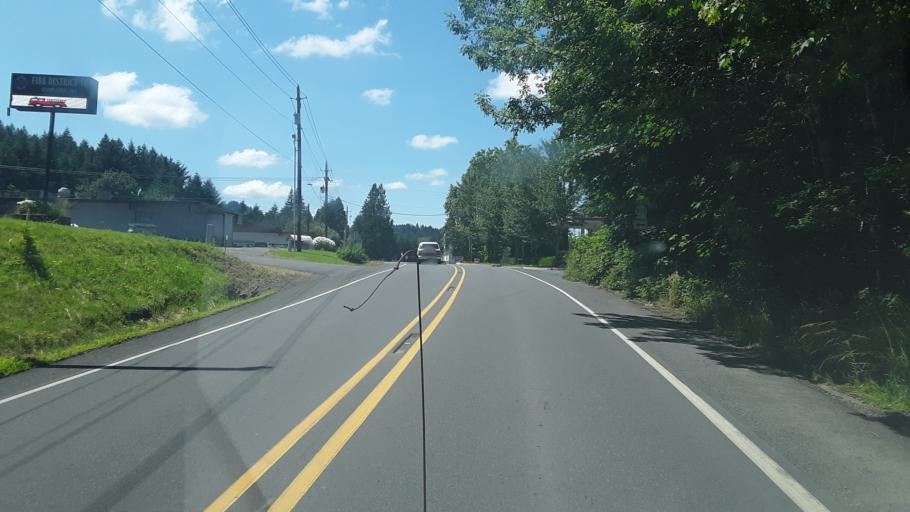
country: US
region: Washington
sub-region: Clark County
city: Amboy
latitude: 45.9100
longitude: -122.4507
